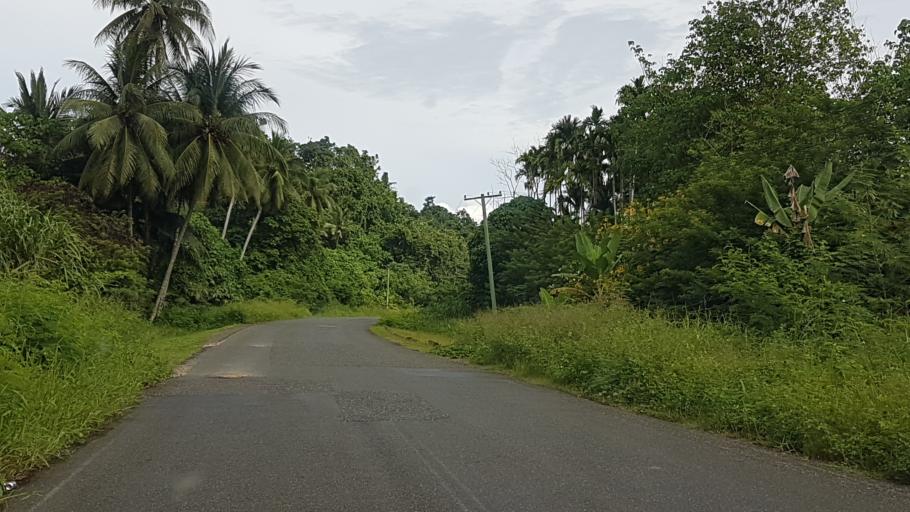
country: PG
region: Madang
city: Madang
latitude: -5.0503
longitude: 145.8019
